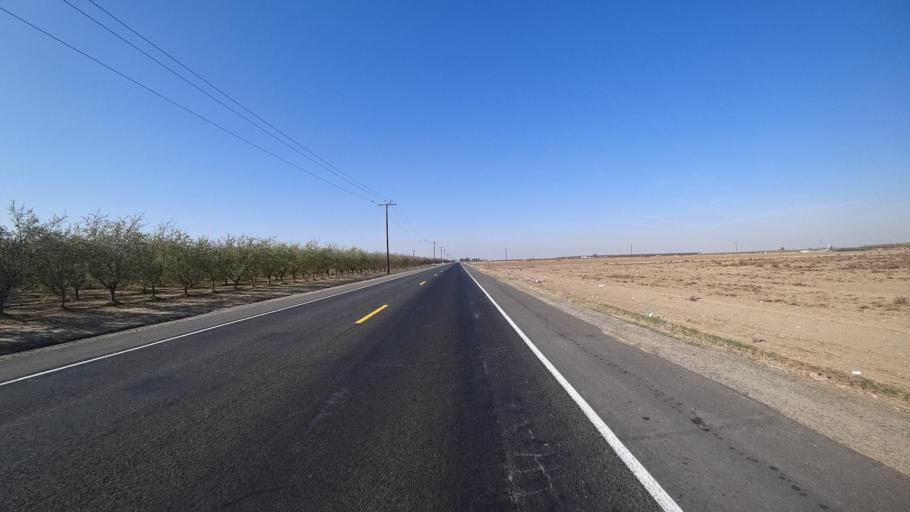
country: US
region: California
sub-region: Kern County
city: McFarland
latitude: 35.7179
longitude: -119.2464
